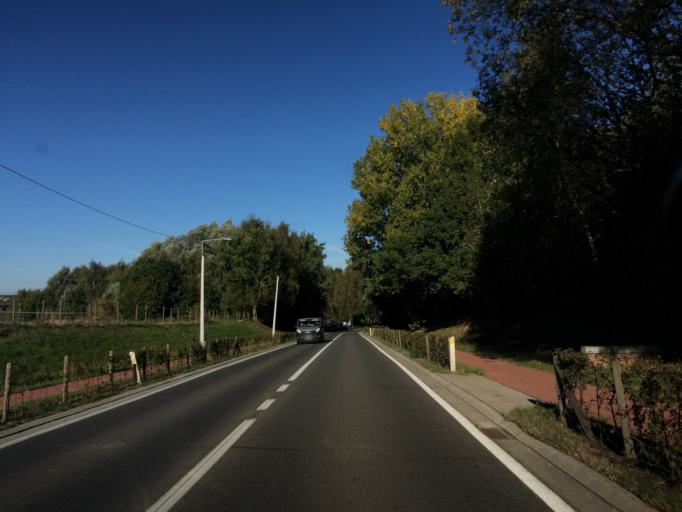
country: BE
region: Flanders
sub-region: Provincie Vlaams-Brabant
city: Merchtem
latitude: 50.9323
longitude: 4.2544
